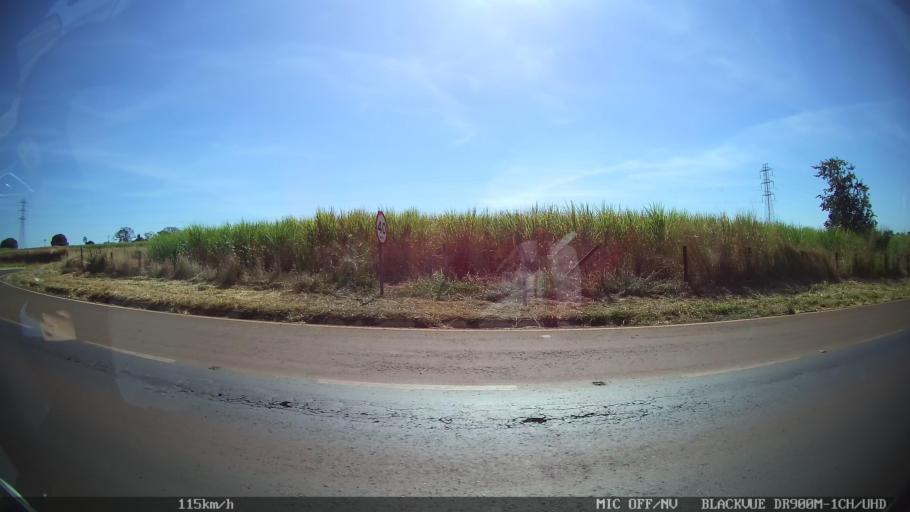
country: BR
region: Sao Paulo
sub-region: Barretos
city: Barretos
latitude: -20.5055
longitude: -48.5502
